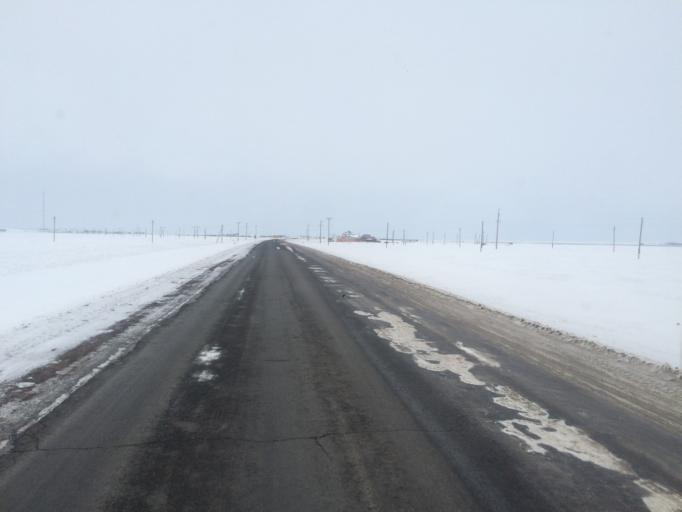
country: RU
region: Orenburg
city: Dombarovskiy
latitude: 49.9566
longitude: 60.0847
